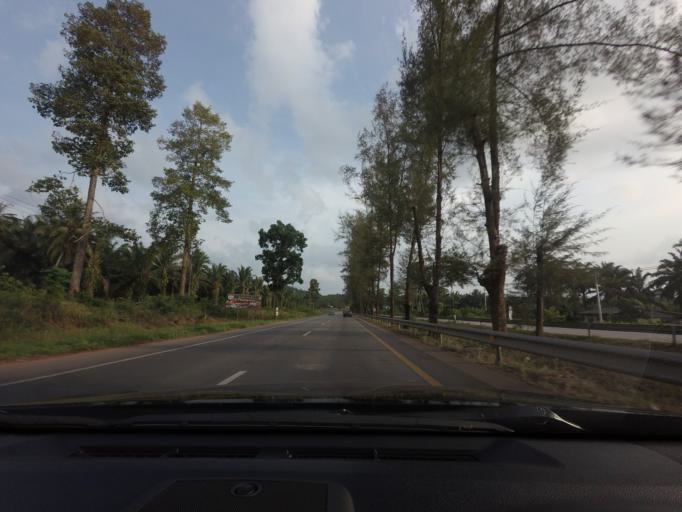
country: TH
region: Chumphon
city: Lang Suan
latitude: 9.8964
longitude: 99.0635
